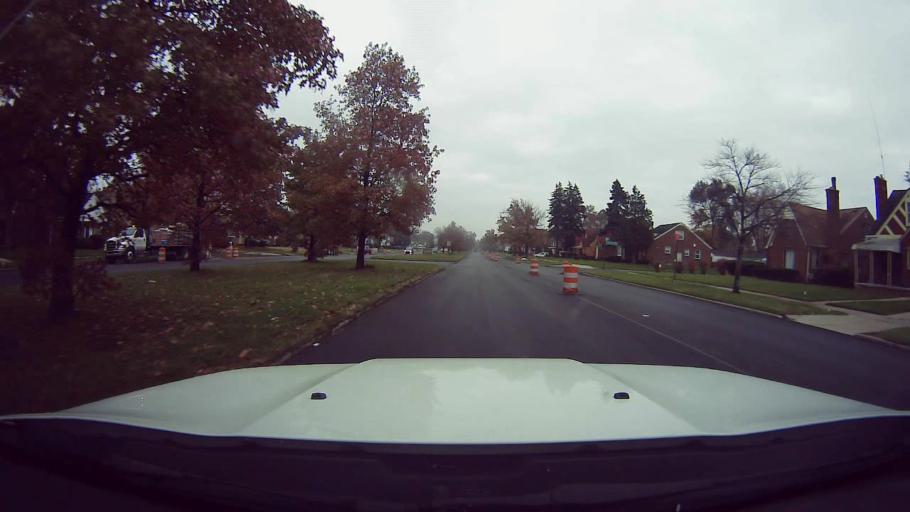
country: US
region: Michigan
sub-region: Oakland County
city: Oak Park
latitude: 42.4194
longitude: -83.2086
